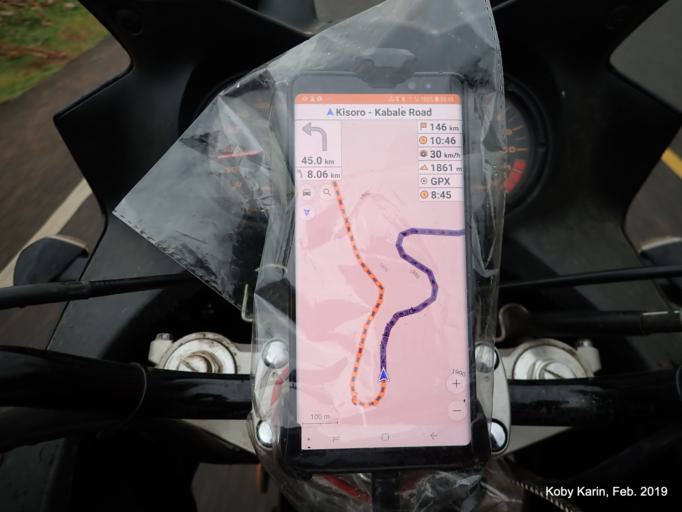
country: UG
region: Western Region
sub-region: Kabale District
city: Kabale
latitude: -1.1173
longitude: 29.8948
